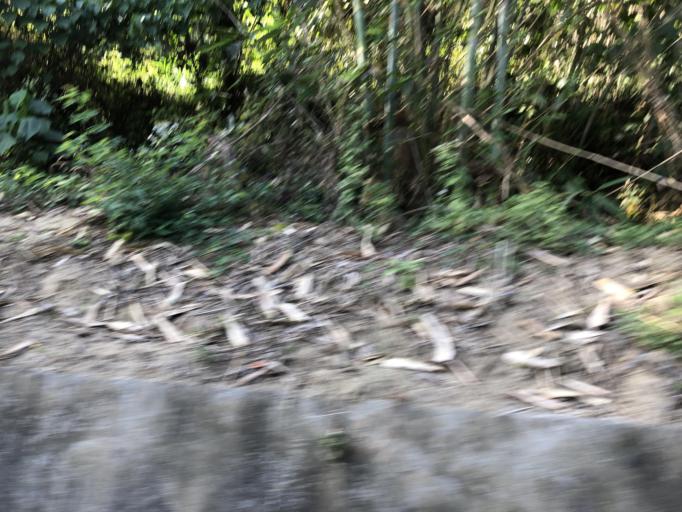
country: TW
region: Taiwan
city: Yujing
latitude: 23.0203
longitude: 120.3838
